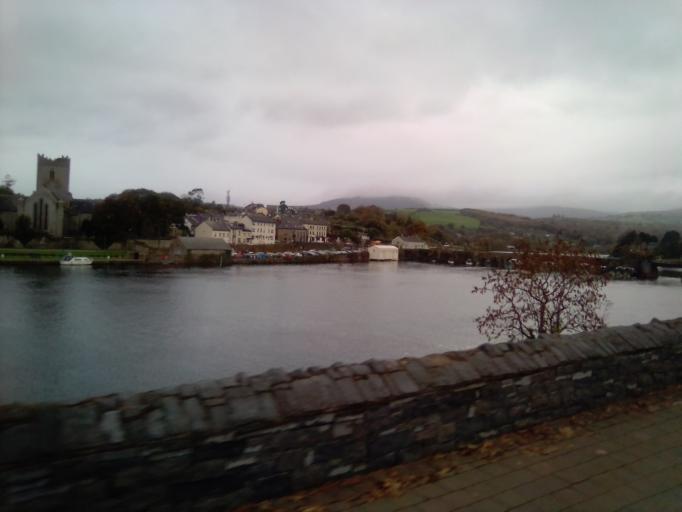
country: IE
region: Munster
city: Ballina
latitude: 52.8072
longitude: -8.4361
